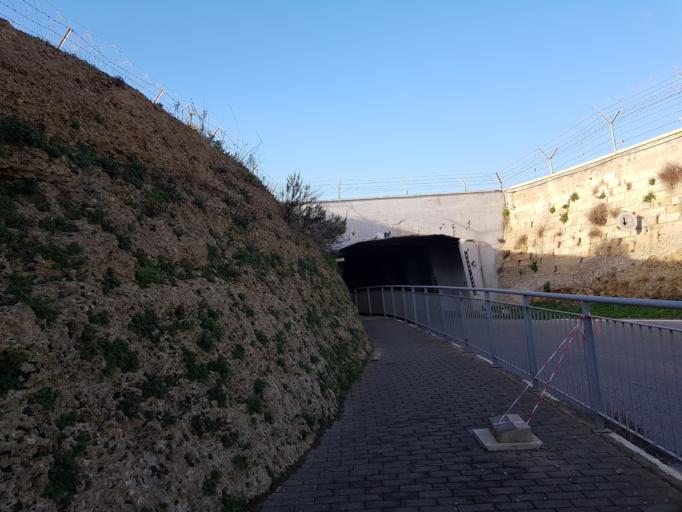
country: IT
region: Apulia
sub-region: Provincia di Brindisi
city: Materdomini
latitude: 40.6528
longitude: 17.9516
